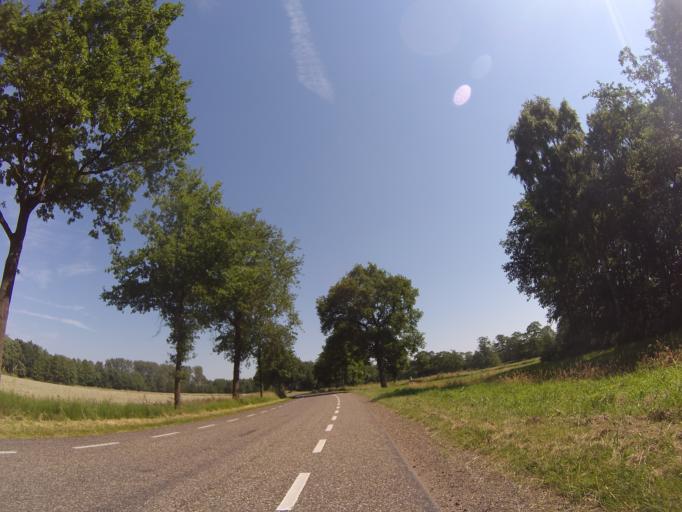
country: NL
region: Drenthe
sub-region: Gemeente Coevorden
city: Sleen
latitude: 52.8056
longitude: 6.7333
